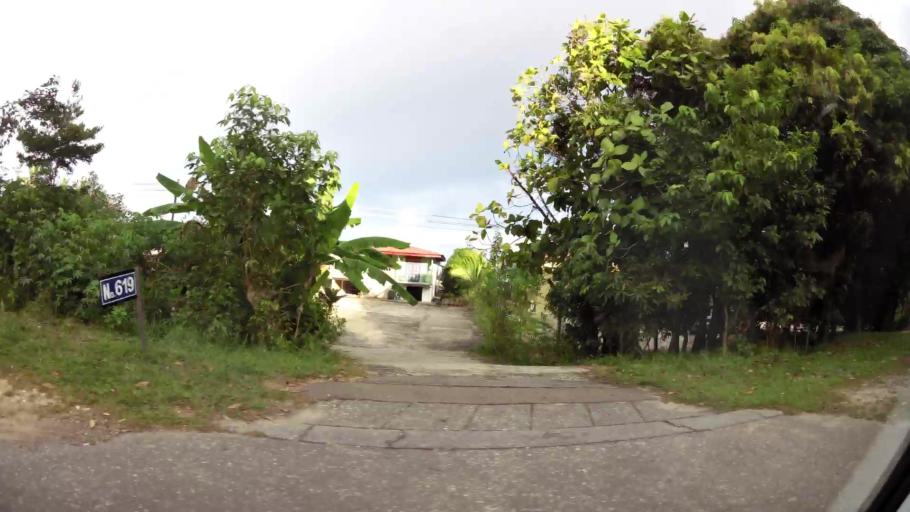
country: BN
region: Brunei and Muara
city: Bandar Seri Begawan
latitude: 4.9377
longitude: 115.0182
